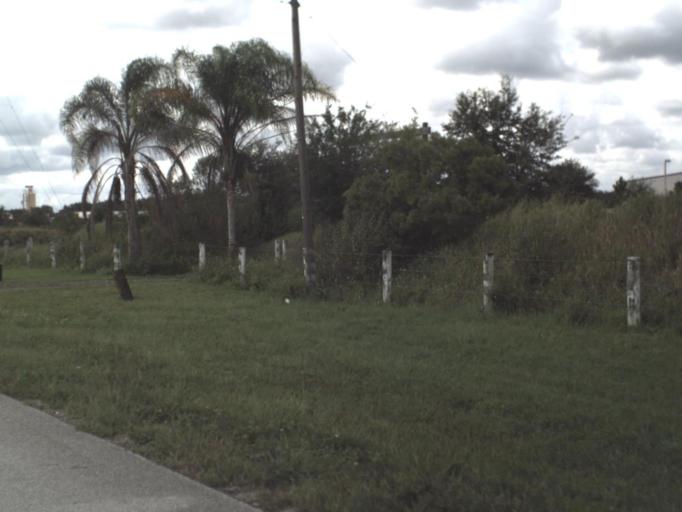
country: US
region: Florida
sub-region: DeSoto County
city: Nocatee
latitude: 27.2015
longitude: -81.9405
